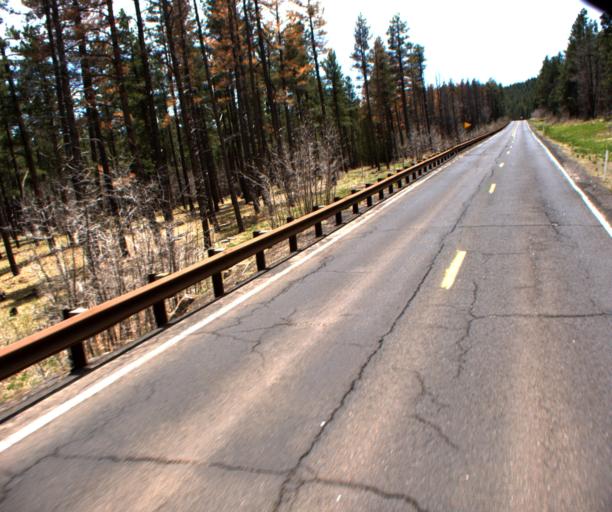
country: US
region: Arizona
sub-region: Coconino County
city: Kachina Village
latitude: 35.0707
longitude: -111.7316
